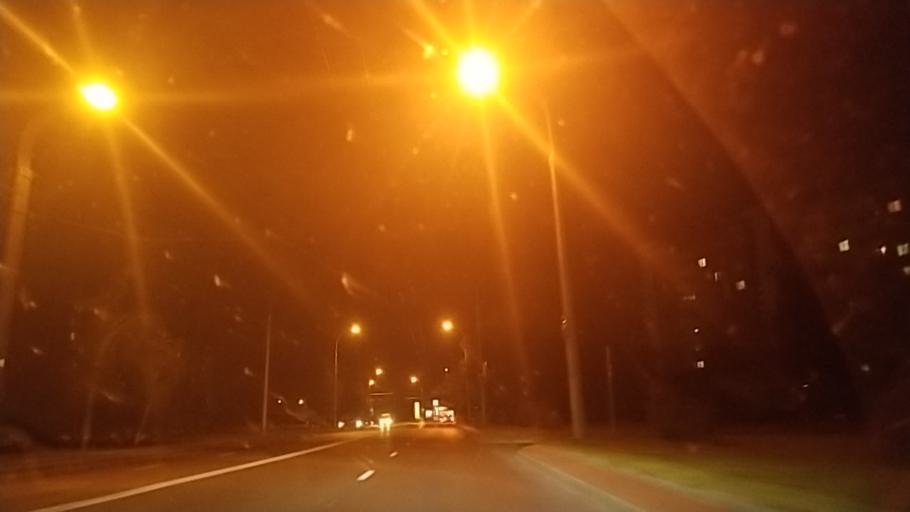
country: BY
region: Brest
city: Brest
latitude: 52.0714
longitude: 23.7588
